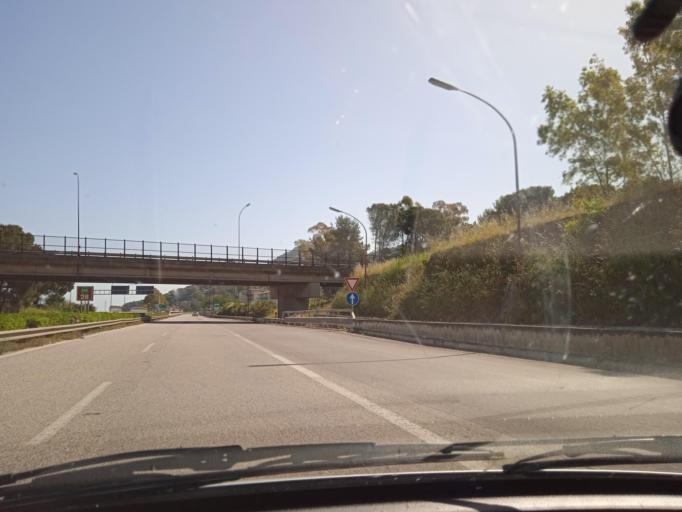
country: IT
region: Sicily
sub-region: Messina
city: Brolo
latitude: 38.1482
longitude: 14.8284
